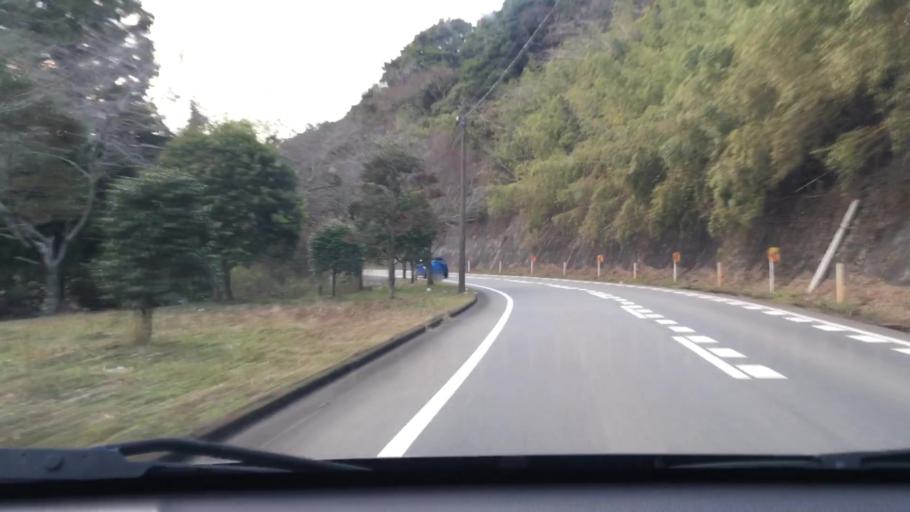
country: JP
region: Oita
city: Hiji
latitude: 33.3706
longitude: 131.4638
